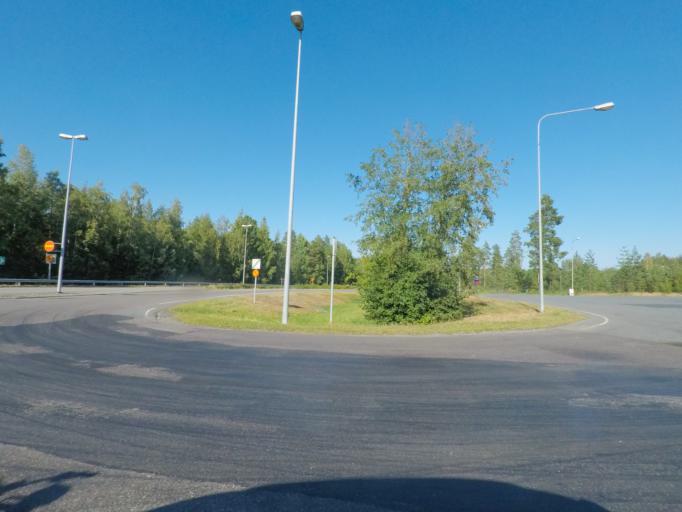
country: FI
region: Paijanne Tavastia
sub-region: Lahti
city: Heinola
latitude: 61.2198
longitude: 26.0133
